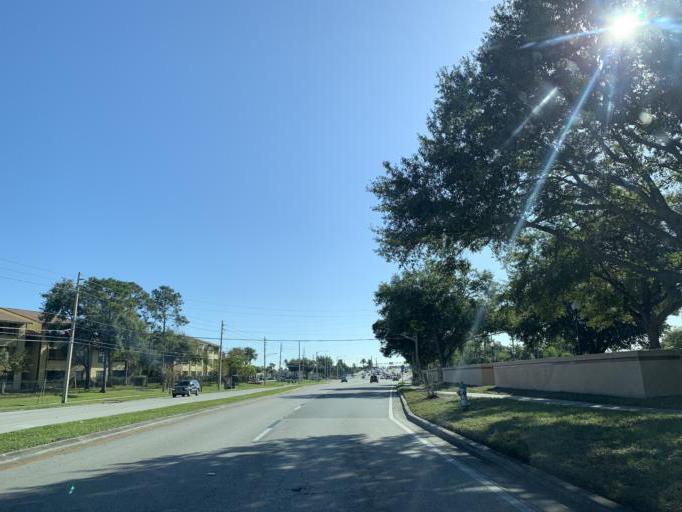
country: US
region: Florida
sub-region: Orange County
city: Oak Ridge
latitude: 28.4965
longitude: -81.4390
